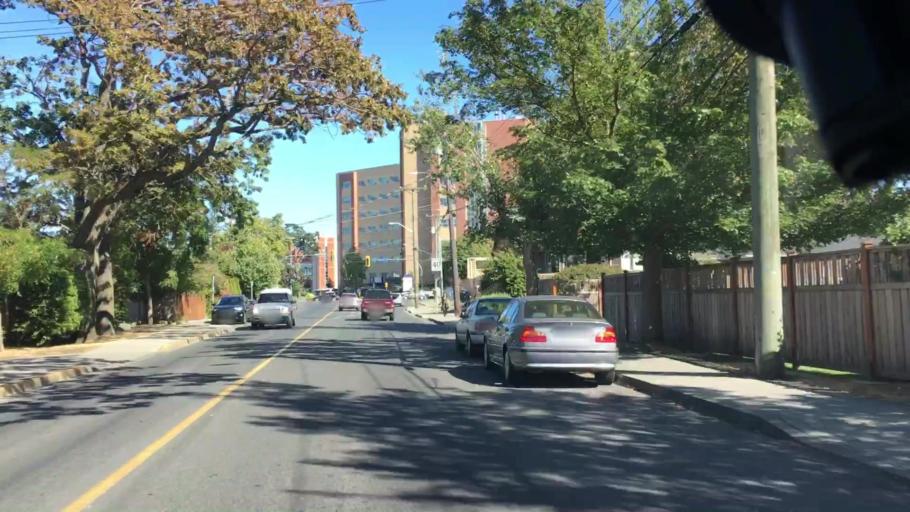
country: CA
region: British Columbia
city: Oak Bay
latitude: 48.4337
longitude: -123.3310
